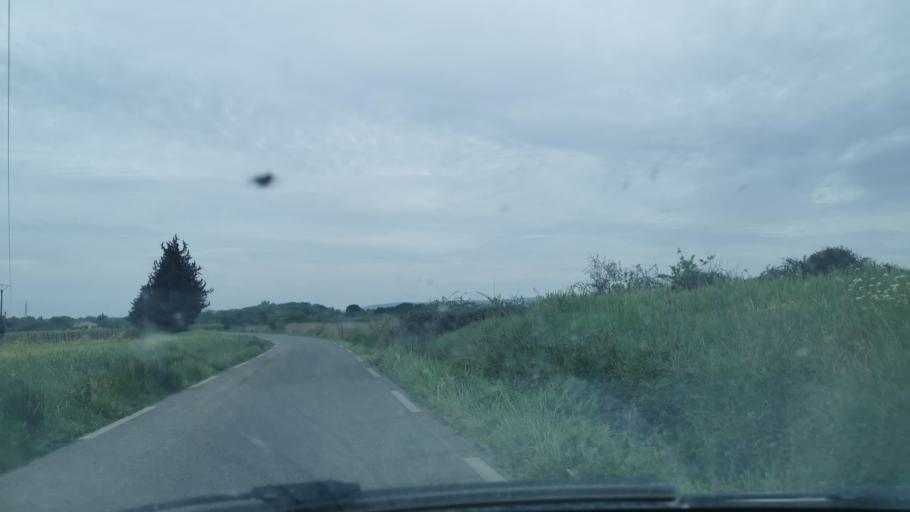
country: FR
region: Languedoc-Roussillon
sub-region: Departement de l'Herault
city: Saussan
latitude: 43.5619
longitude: 3.7725
